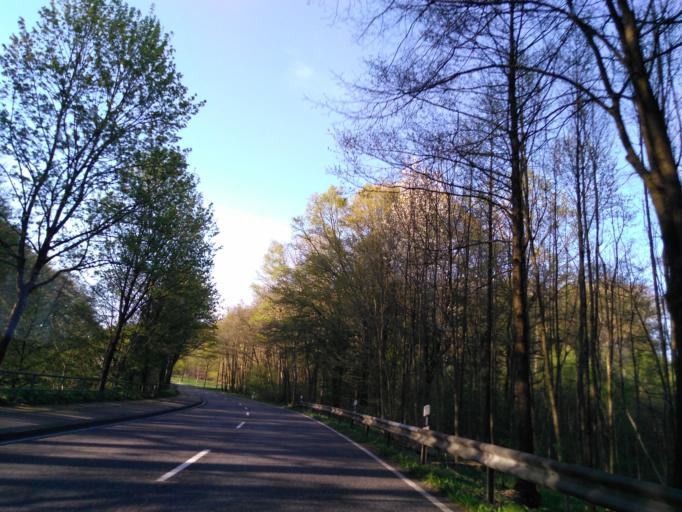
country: DE
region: North Rhine-Westphalia
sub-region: Regierungsbezirk Koln
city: Much
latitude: 50.8977
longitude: 7.3918
